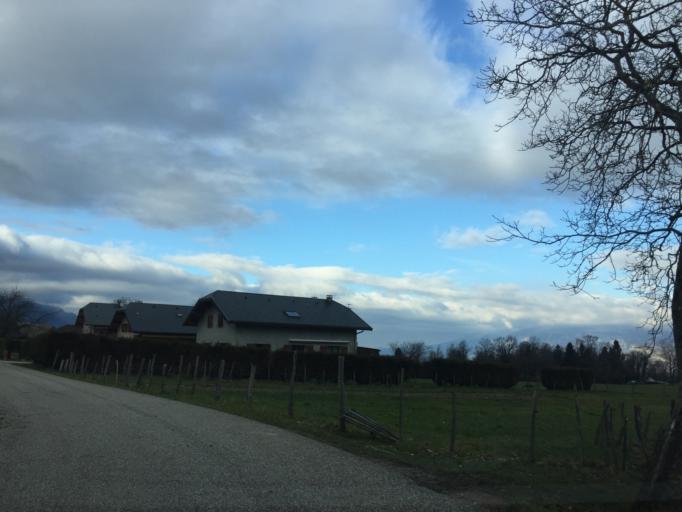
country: FR
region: Rhone-Alpes
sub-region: Departement de la Savoie
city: Vimines
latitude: 45.5554
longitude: 5.8512
